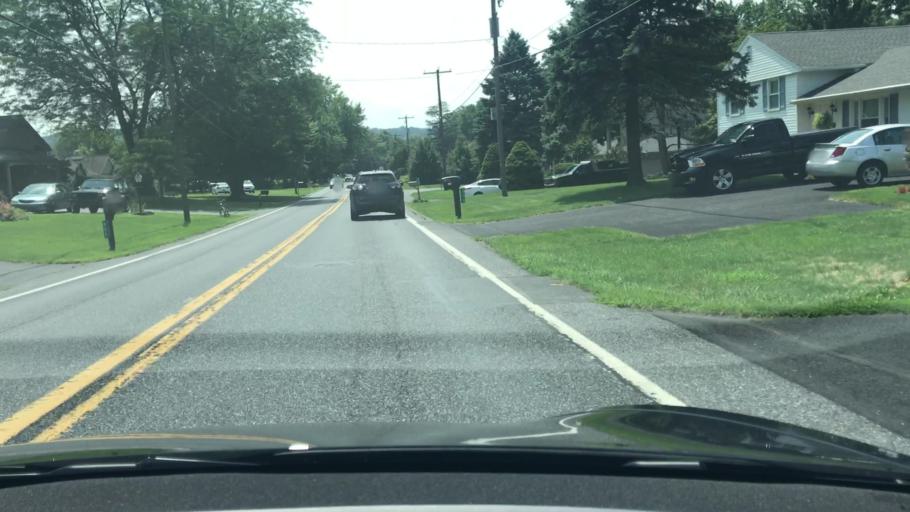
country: US
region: Pennsylvania
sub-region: Lancaster County
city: Landisville
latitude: 40.0739
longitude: -76.4087
